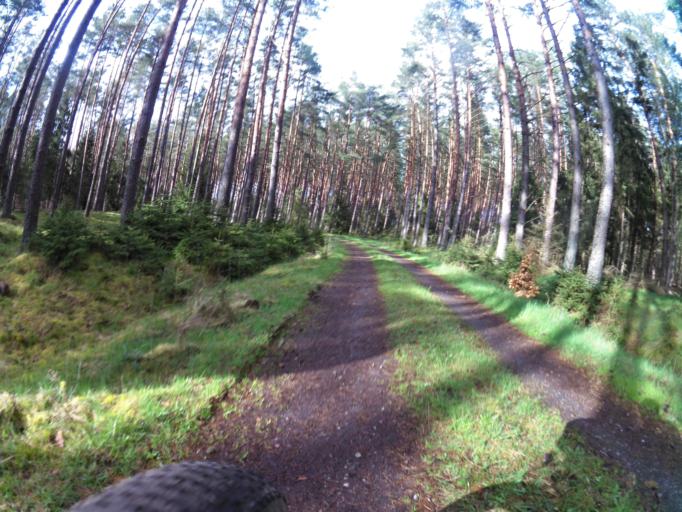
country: PL
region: Pomeranian Voivodeship
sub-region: Powiat slupski
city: Kepice
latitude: 54.2943
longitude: 16.8359
